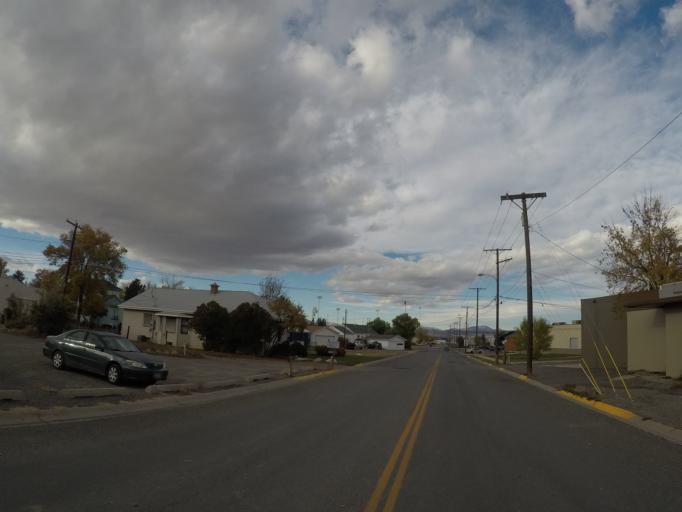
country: US
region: Montana
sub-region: Lewis and Clark County
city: Helena
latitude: 46.5965
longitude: -112.0259
